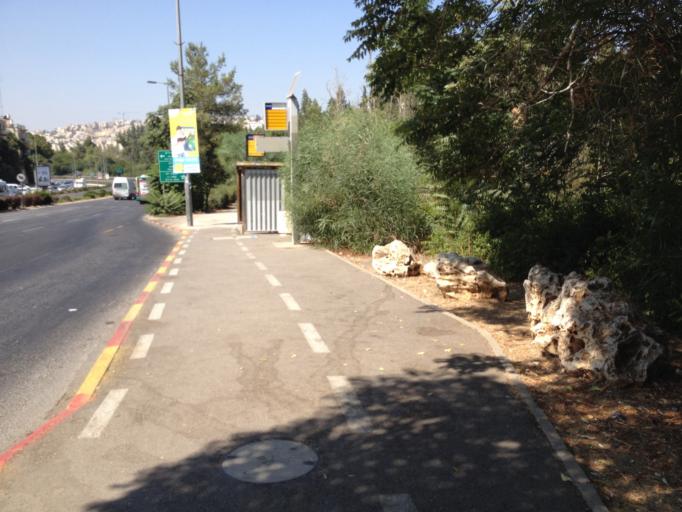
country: IL
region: Jerusalem
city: Jerusalem
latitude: 31.7697
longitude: 35.2083
